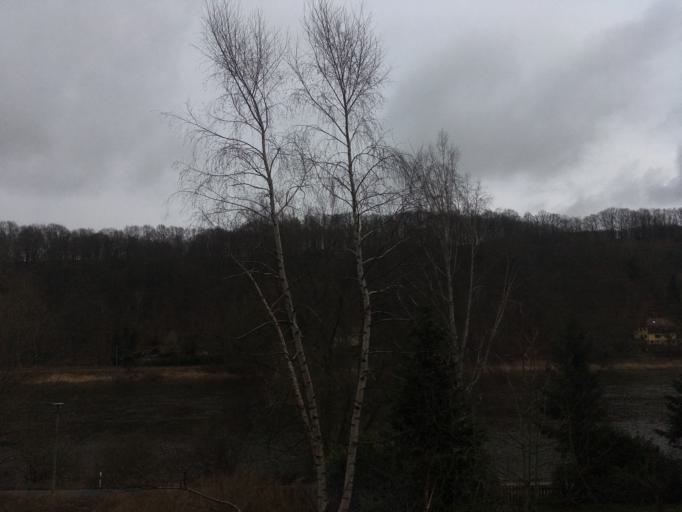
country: DE
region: Saxony
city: Pirna
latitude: 50.9587
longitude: 13.9719
